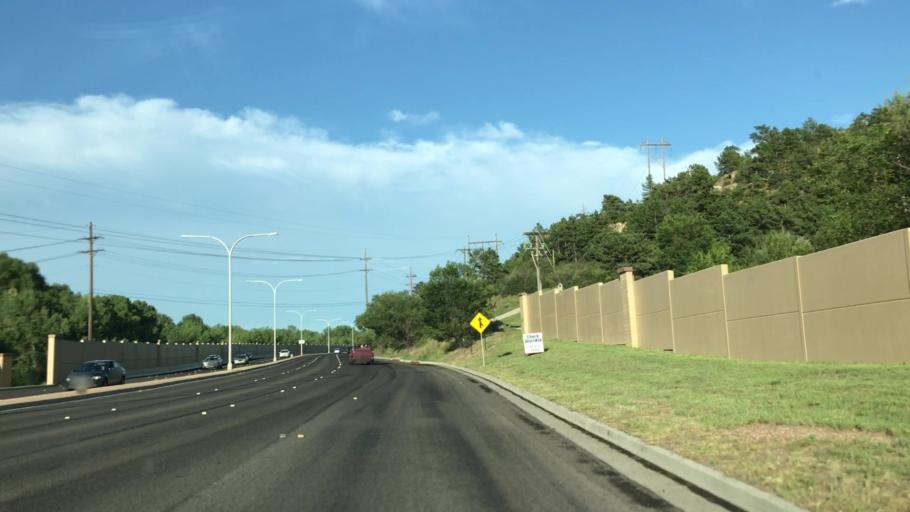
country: US
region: Colorado
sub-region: El Paso County
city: Colorado Springs
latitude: 38.8890
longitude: -104.7826
